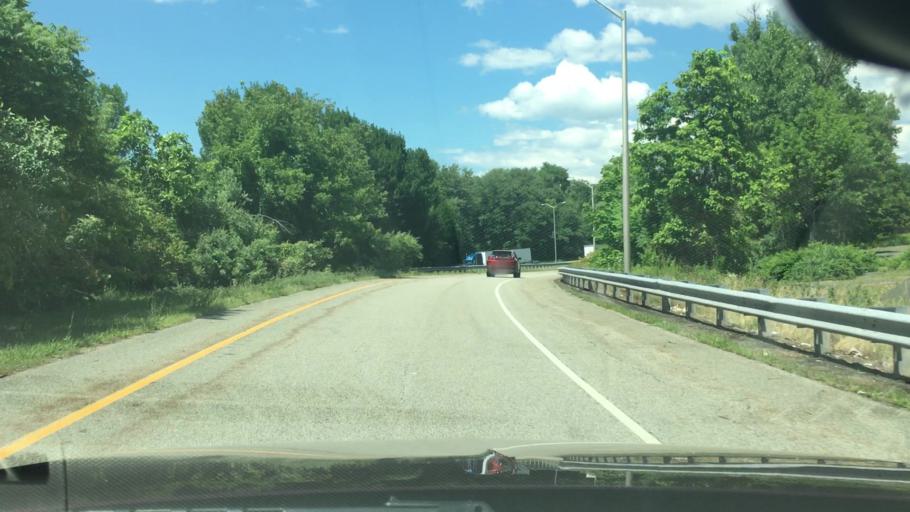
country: US
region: Connecticut
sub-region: Hartford County
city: Windsor Locks
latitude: 41.9193
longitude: -72.6122
